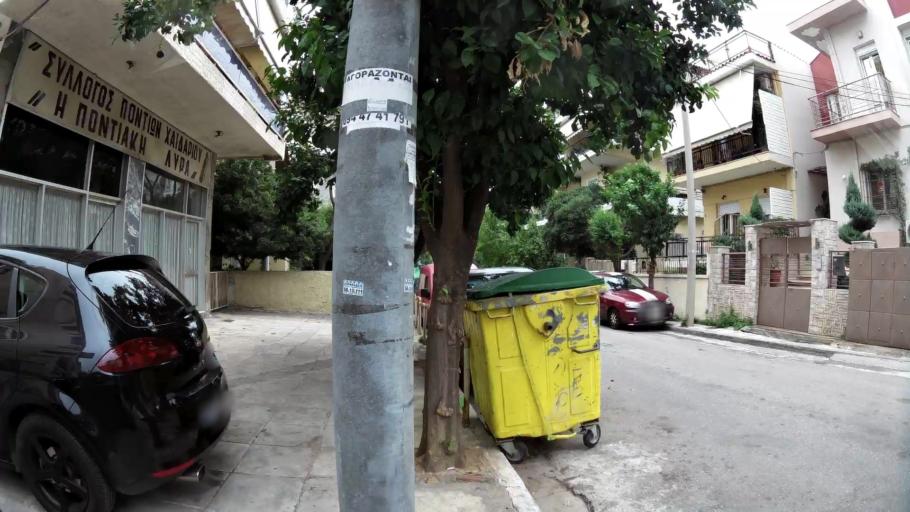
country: GR
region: Attica
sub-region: Nomarchia Athinas
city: Chaidari
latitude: 38.0054
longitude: 23.6650
